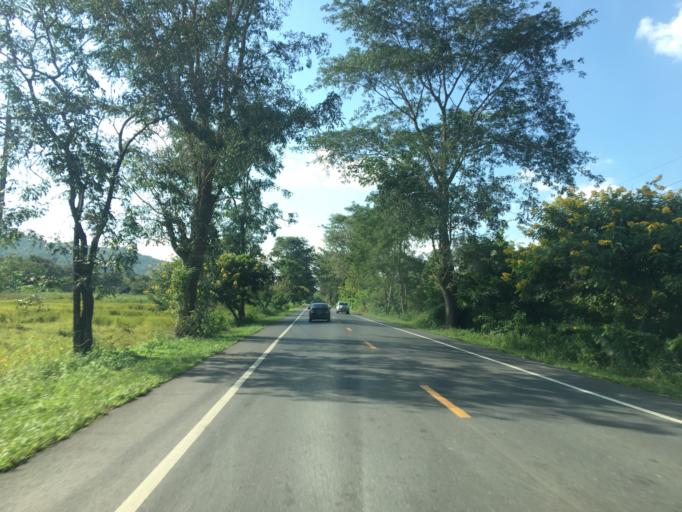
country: TH
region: Phayao
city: Chun
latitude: 19.3524
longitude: 100.1031
